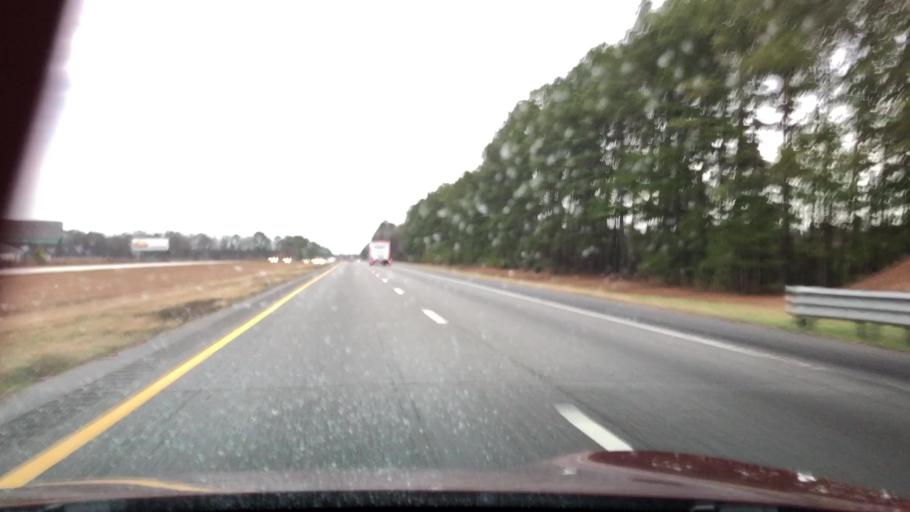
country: US
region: South Carolina
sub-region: Dillon County
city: Latta
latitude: 34.3853
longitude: -79.4682
